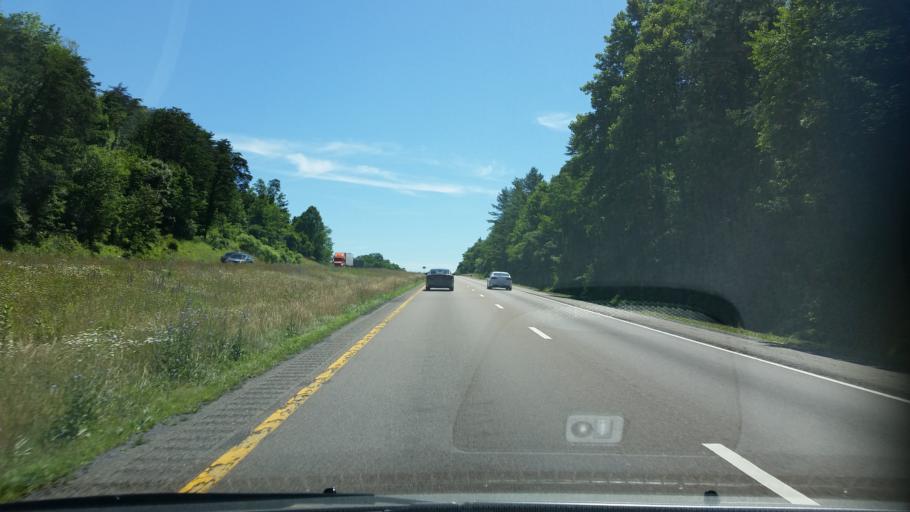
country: US
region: Virginia
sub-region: Smyth County
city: Adwolf
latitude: 36.8128
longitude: -81.6025
